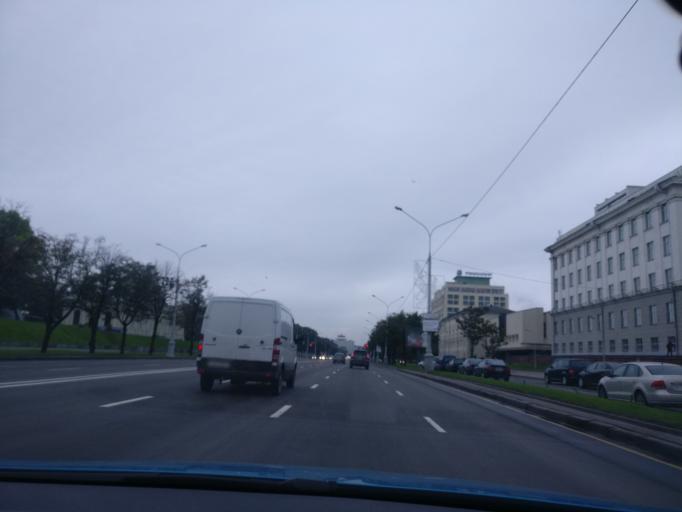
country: BY
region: Minsk
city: Minsk
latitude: 53.9268
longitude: 27.6232
